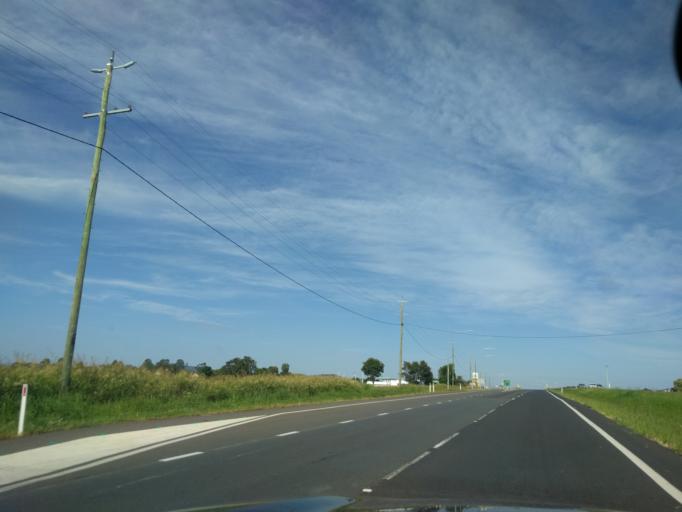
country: AU
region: Queensland
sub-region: Ipswich
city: Thagoona
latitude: -27.5690
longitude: 152.6268
